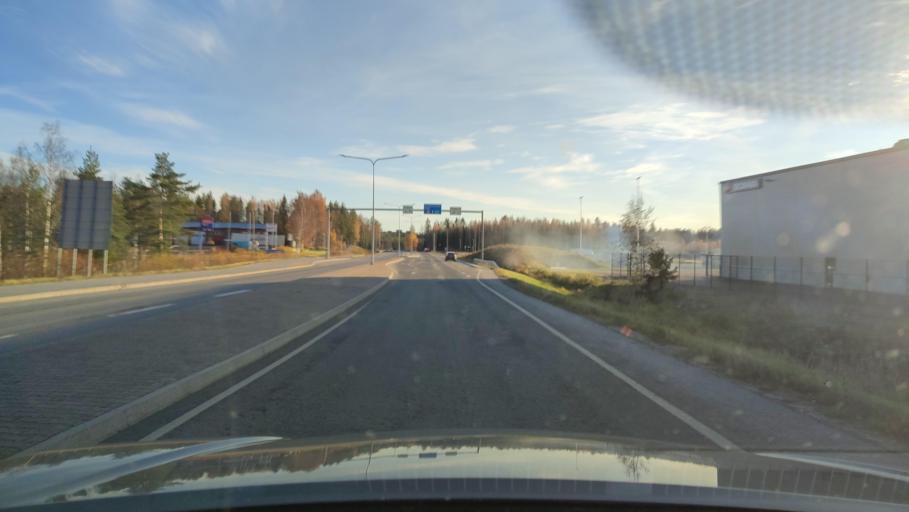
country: FI
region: Ostrobothnia
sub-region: Vaasa
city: Ristinummi
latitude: 63.0264
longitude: 21.7564
